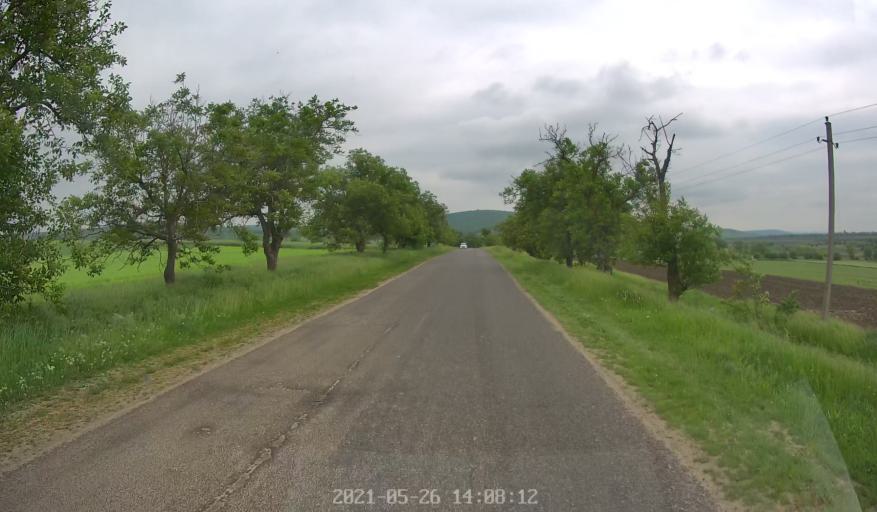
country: MD
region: Hincesti
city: Dancu
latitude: 46.7397
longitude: 28.3588
